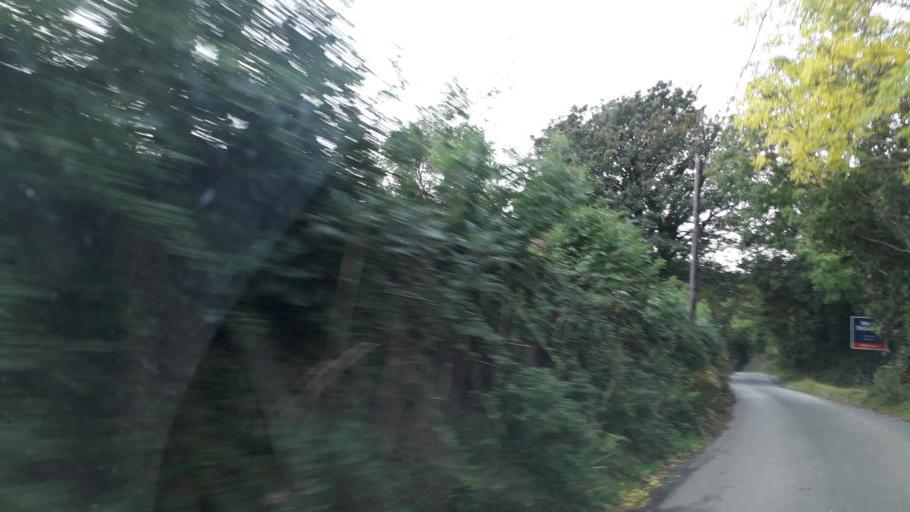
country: IE
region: Leinster
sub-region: Wicklow
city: Enniskerry
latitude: 53.1639
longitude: -6.2111
